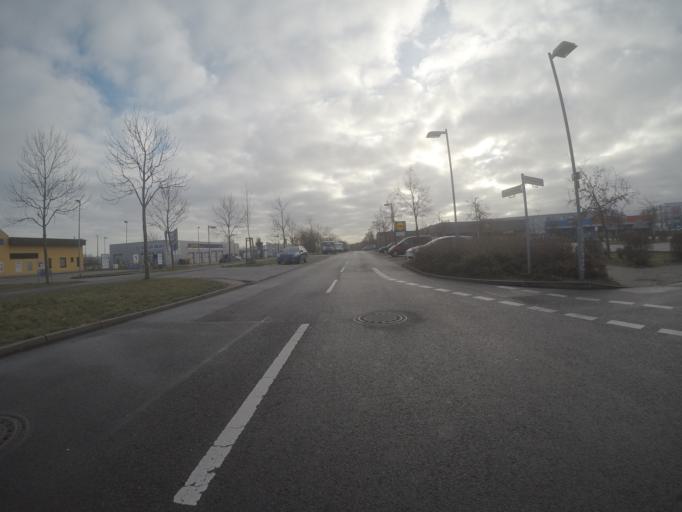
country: DE
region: Berlin
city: Marzahn
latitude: 52.5465
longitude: 13.5755
